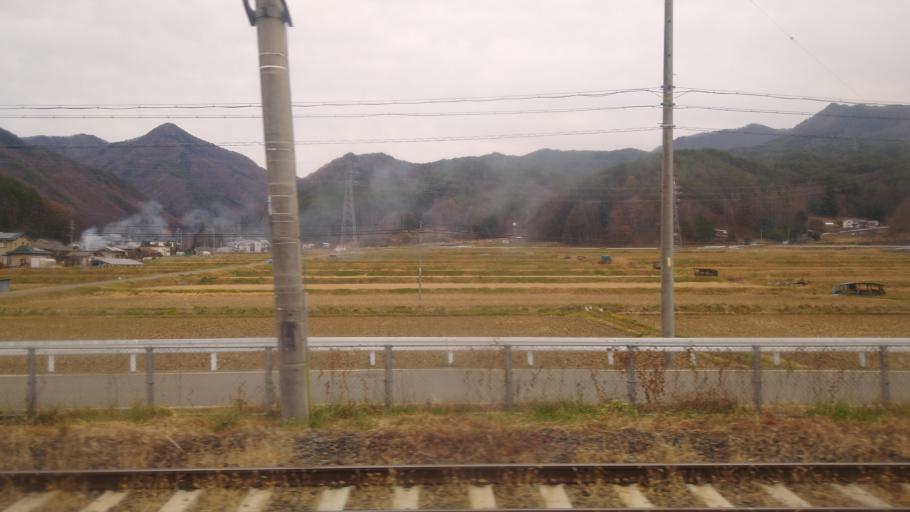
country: JP
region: Nagano
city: Hotaka
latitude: 36.4024
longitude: 138.0143
